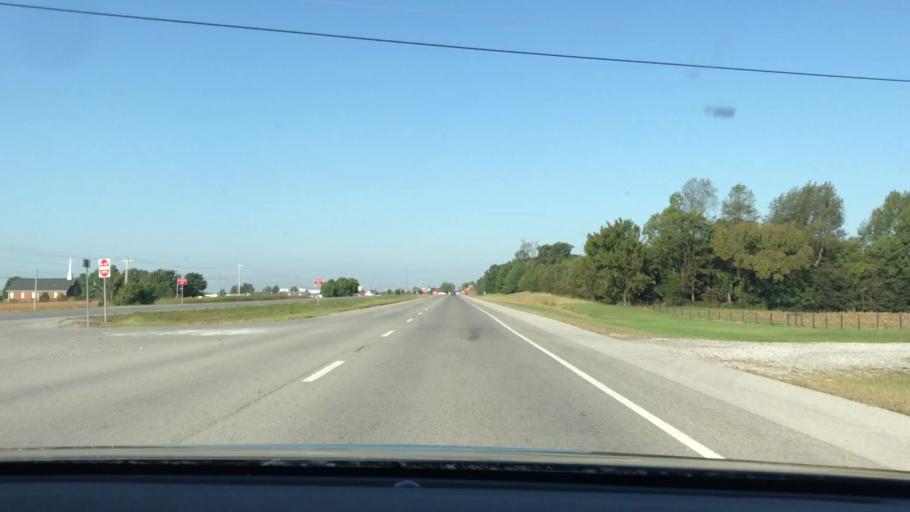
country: US
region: Kentucky
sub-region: Trigg County
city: Cadiz
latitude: 36.8678
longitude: -87.7834
